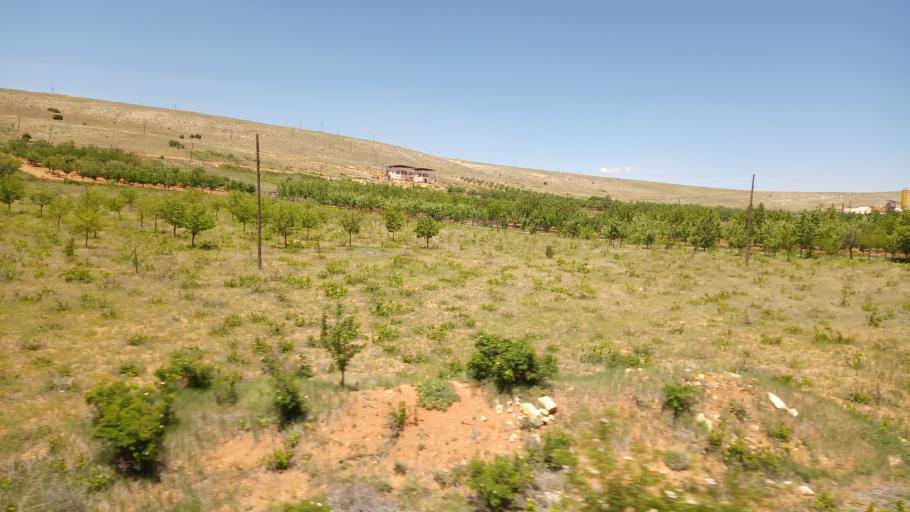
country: TR
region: Malatya
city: Darende
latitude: 38.6010
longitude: 37.4641
